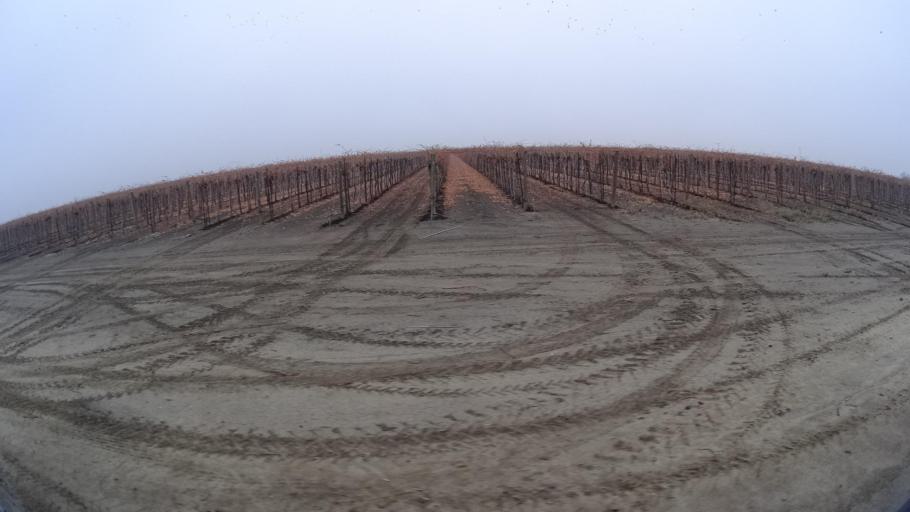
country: US
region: California
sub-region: Kern County
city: Buttonwillow
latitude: 35.4269
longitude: -119.5162
